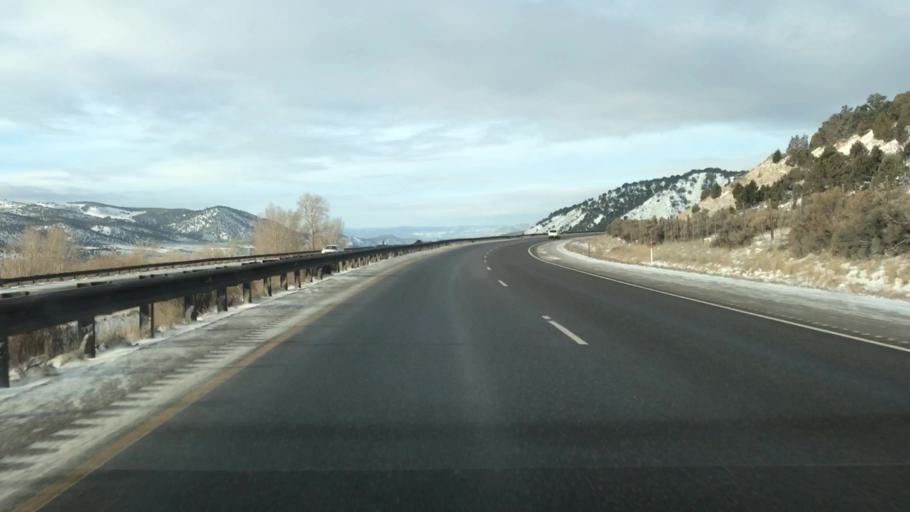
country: US
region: Colorado
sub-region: Eagle County
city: Eagle
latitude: 39.6789
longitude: -106.7661
